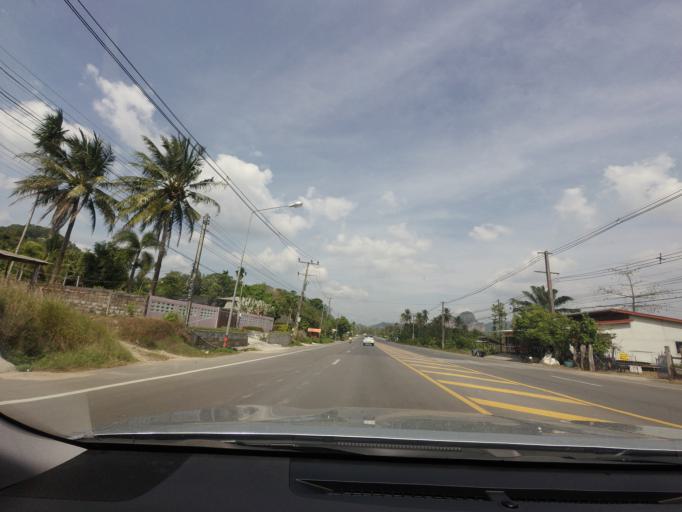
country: TH
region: Phangnga
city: Ban Ao Nang
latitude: 8.0532
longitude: 98.7749
